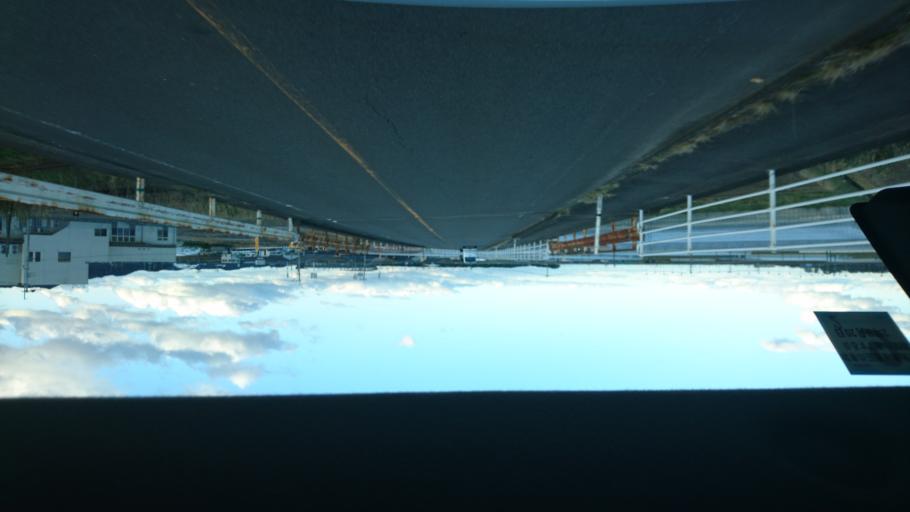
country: JP
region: Miyazaki
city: Miyazaki-shi
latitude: 31.8400
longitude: 131.4360
